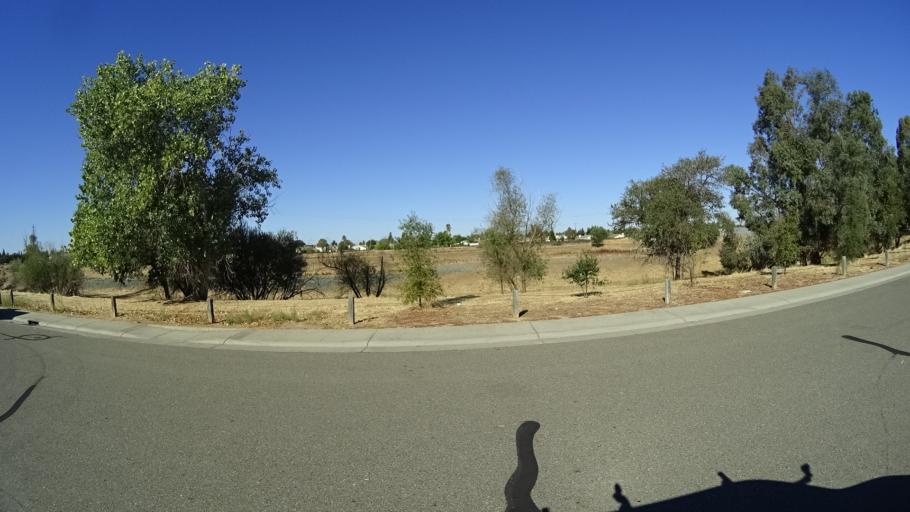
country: US
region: California
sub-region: Sacramento County
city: Vineyard
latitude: 38.4499
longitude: -121.3779
